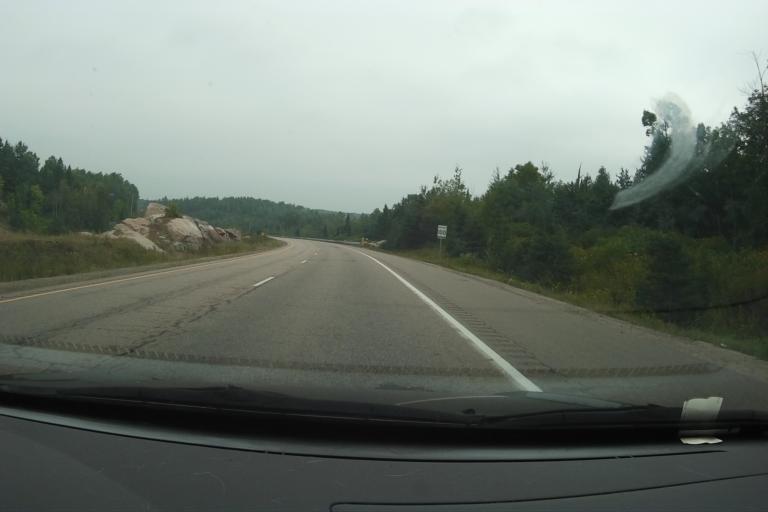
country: CA
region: Ontario
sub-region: Nipissing District
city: North Bay
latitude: 46.2060
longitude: -79.3494
